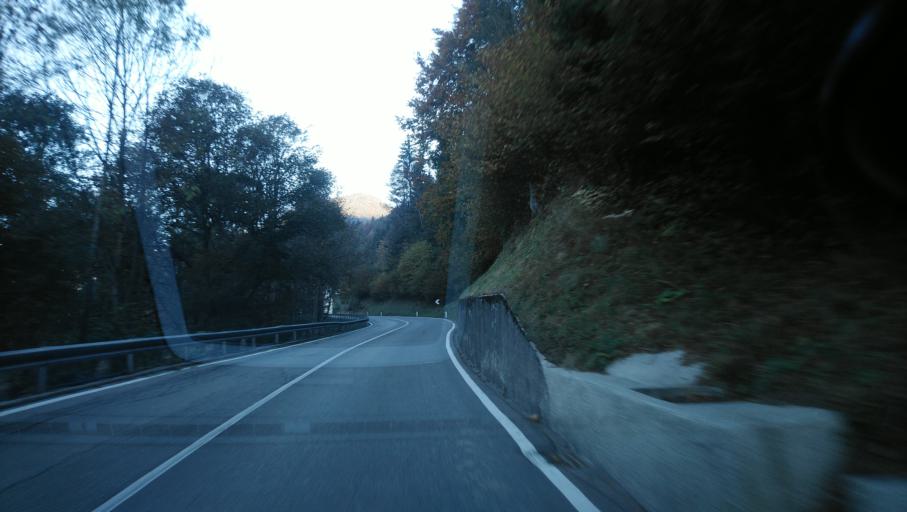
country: IT
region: Veneto
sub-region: Provincia di Belluno
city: Vallada Agordina
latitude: 46.3638
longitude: 11.9481
